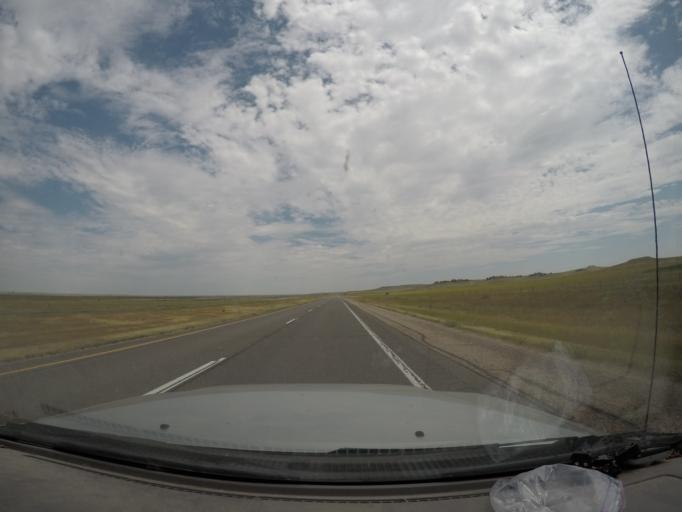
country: US
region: Wyoming
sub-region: Laramie County
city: Pine Bluffs
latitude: 41.1873
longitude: -104.0206
